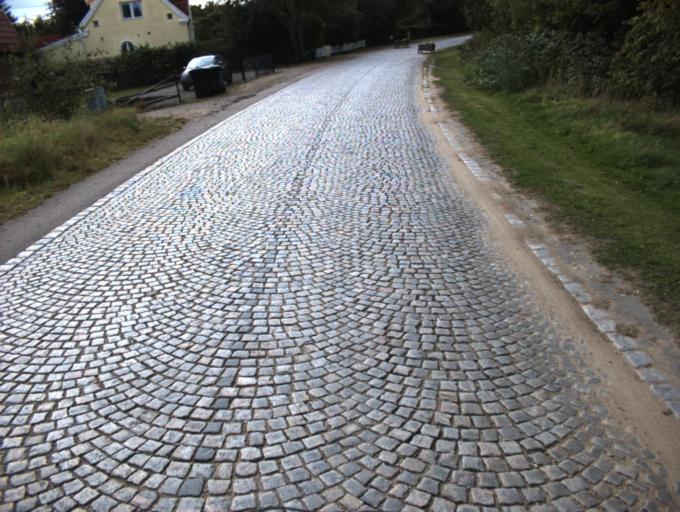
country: SE
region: Skane
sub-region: Helsingborg
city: Odakra
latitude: 56.0852
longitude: 12.7489
